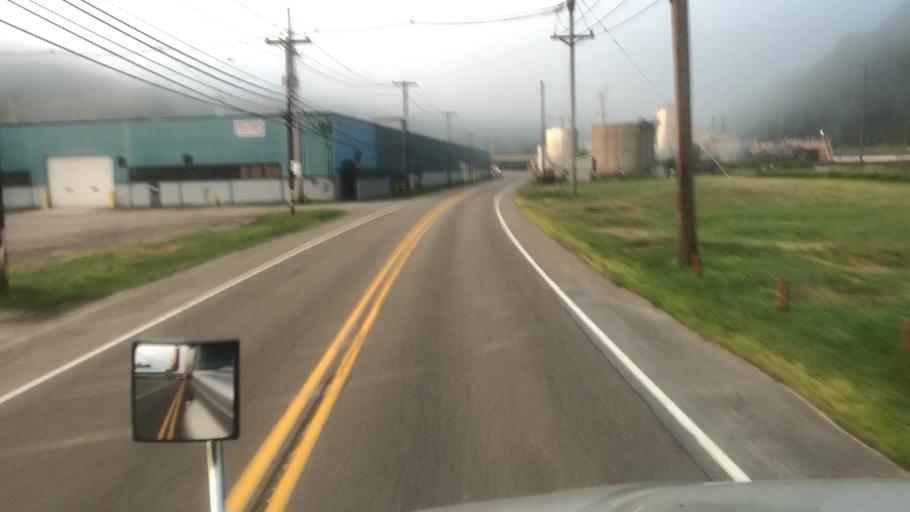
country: US
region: Pennsylvania
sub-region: Venango County
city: Hasson Heights
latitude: 41.4559
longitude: -79.6898
